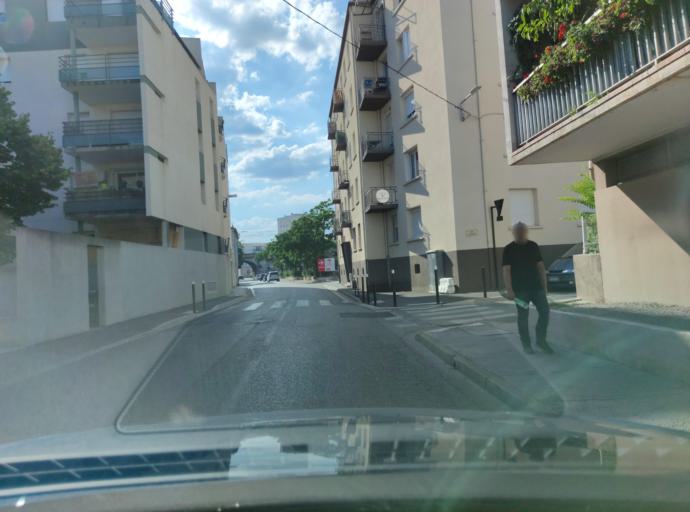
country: FR
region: Languedoc-Roussillon
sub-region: Departement du Gard
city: Nimes
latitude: 43.8364
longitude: 4.3732
